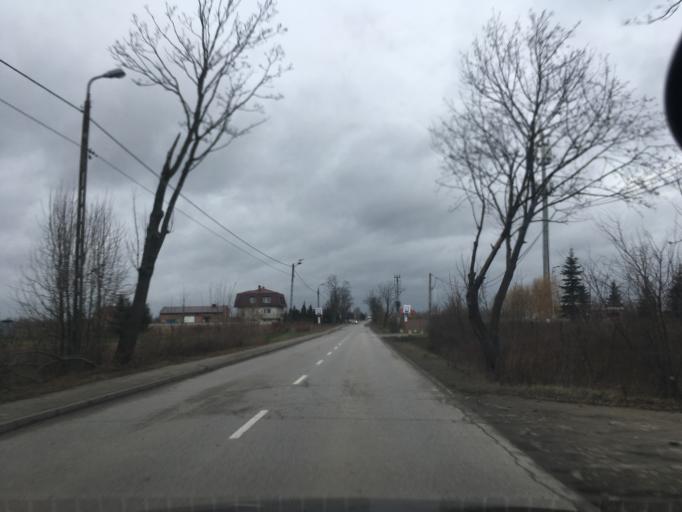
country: PL
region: Masovian Voivodeship
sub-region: Powiat piaseczynski
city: Lesznowola
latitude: 52.1152
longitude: 20.9308
